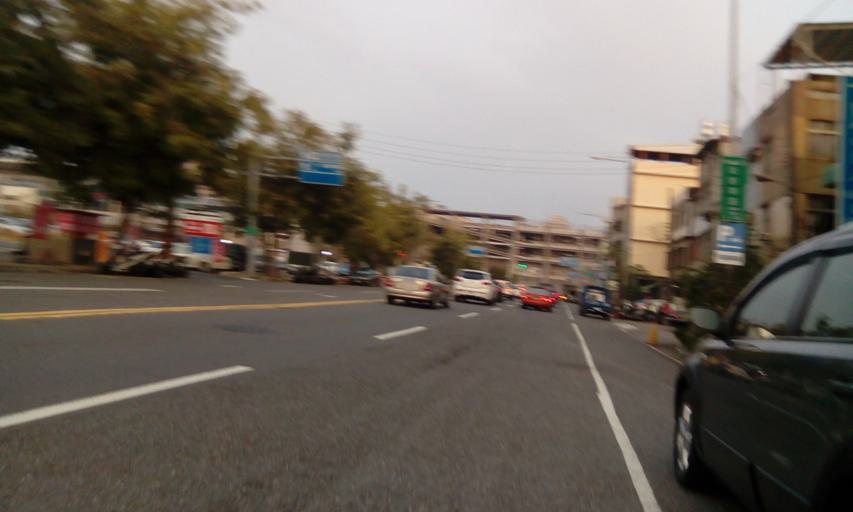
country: TW
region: Kaohsiung
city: Kaohsiung
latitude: 22.6879
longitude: 120.3037
